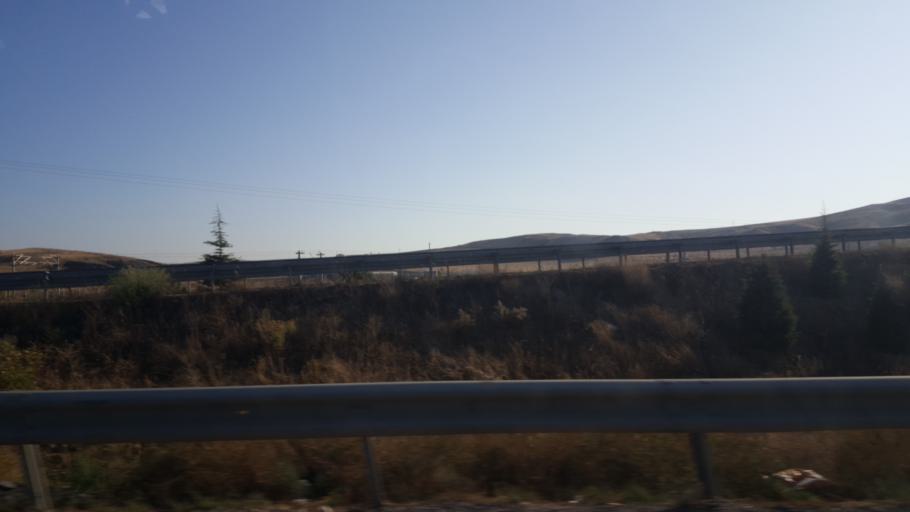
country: TR
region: Ankara
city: Polatli
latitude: 39.5737
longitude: 32.0863
